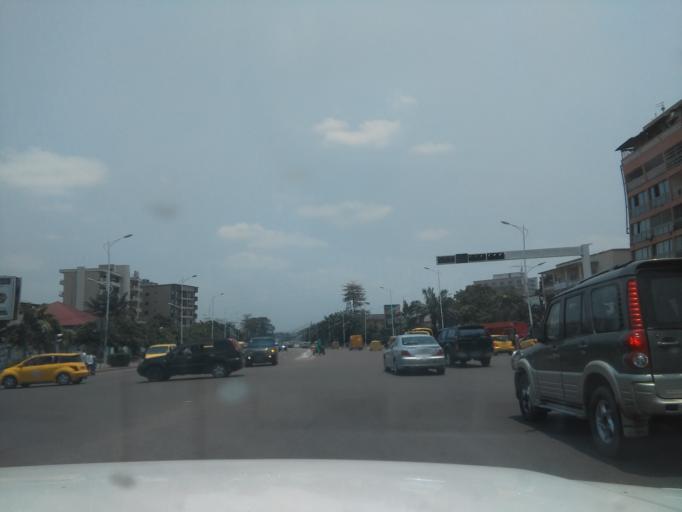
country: CD
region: Kinshasa
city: Kinshasa
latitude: -4.3170
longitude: 15.2789
